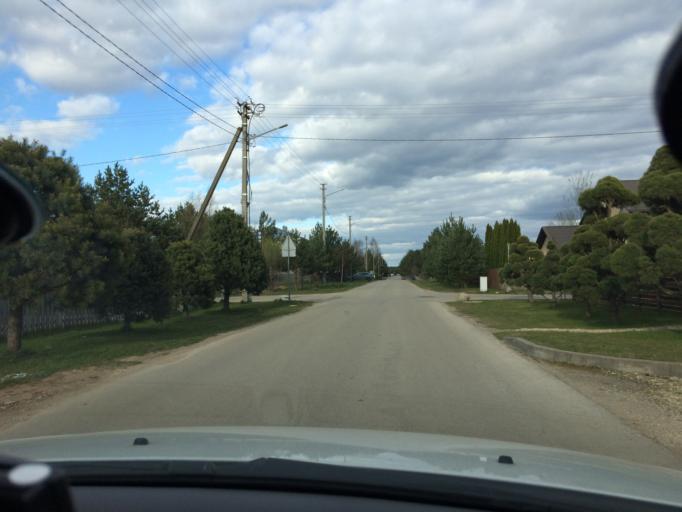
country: LT
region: Vilnius County
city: Rasos
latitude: 54.7750
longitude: 25.3522
